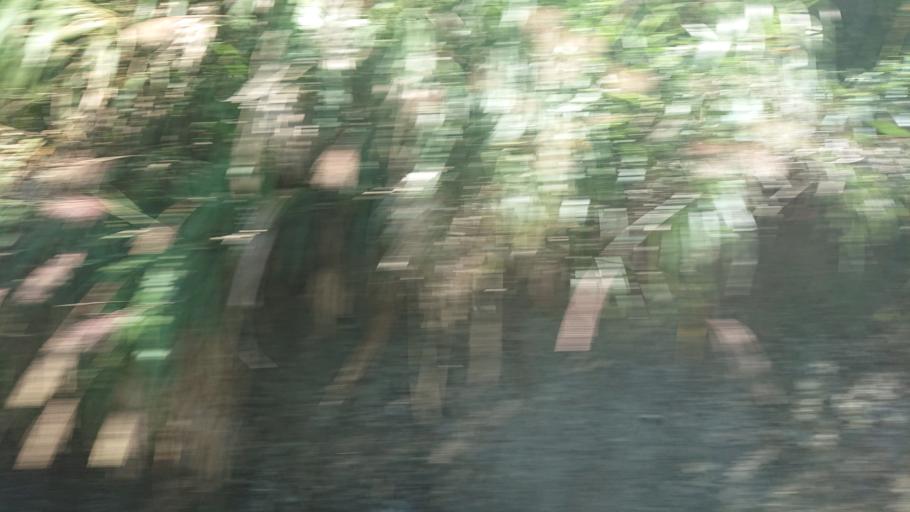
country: TW
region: Taiwan
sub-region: Chiayi
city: Jiayi Shi
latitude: 23.5259
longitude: 120.6317
